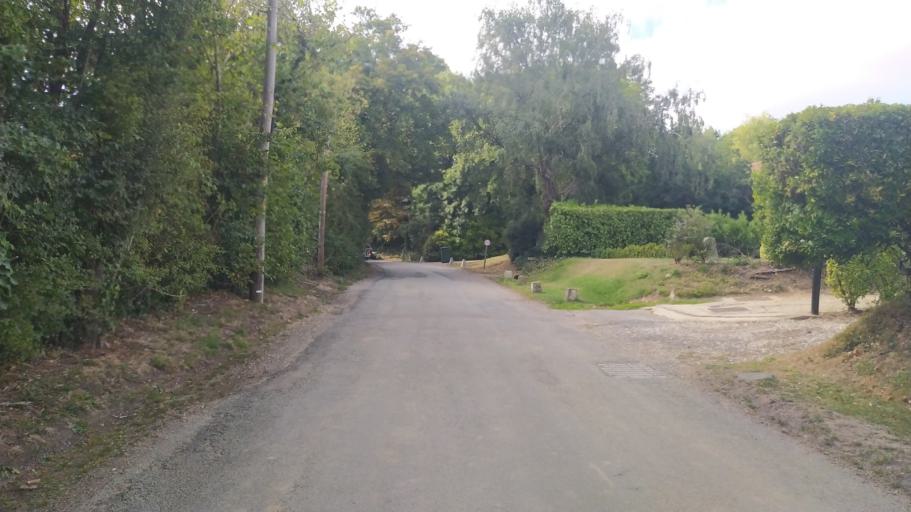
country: GB
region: England
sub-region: West Sussex
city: Chichester
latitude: 50.8084
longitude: -0.7482
